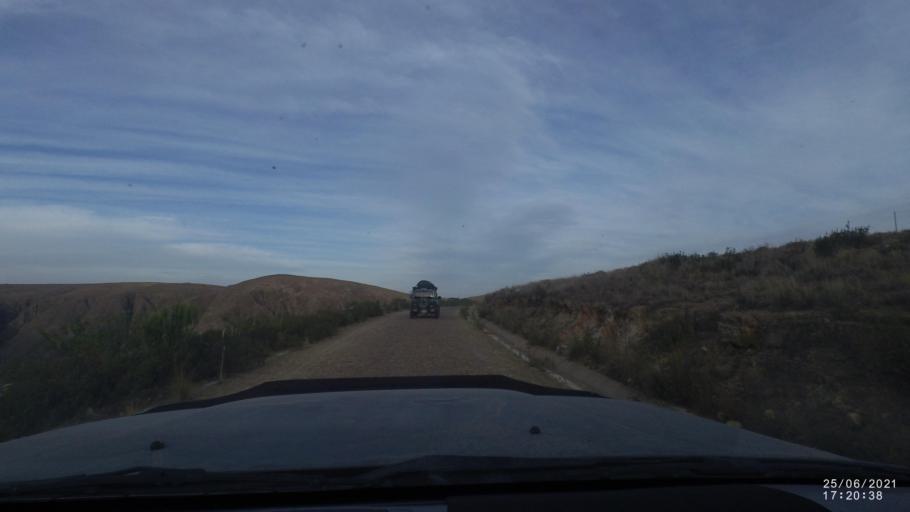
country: BO
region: Cochabamba
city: Arani
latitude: -17.9048
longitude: -65.6881
